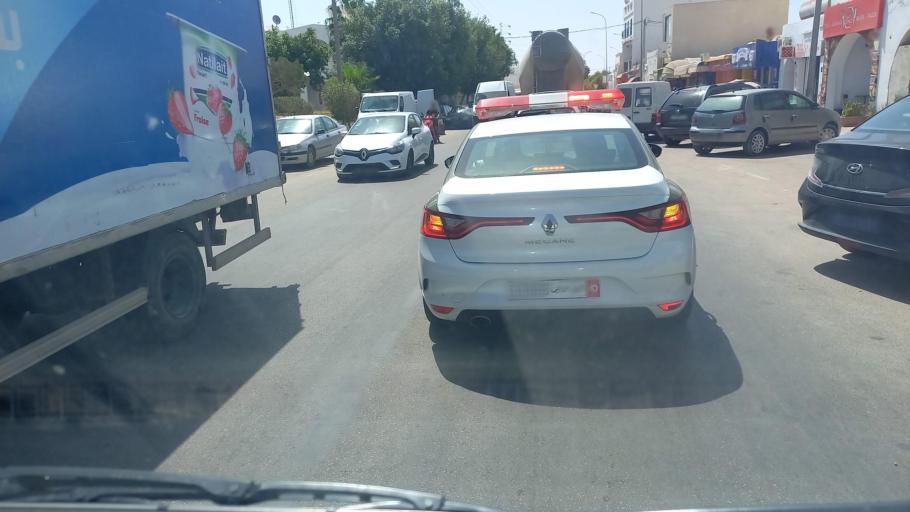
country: TN
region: Madanin
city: Houmt Souk
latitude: 33.8024
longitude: 10.8830
